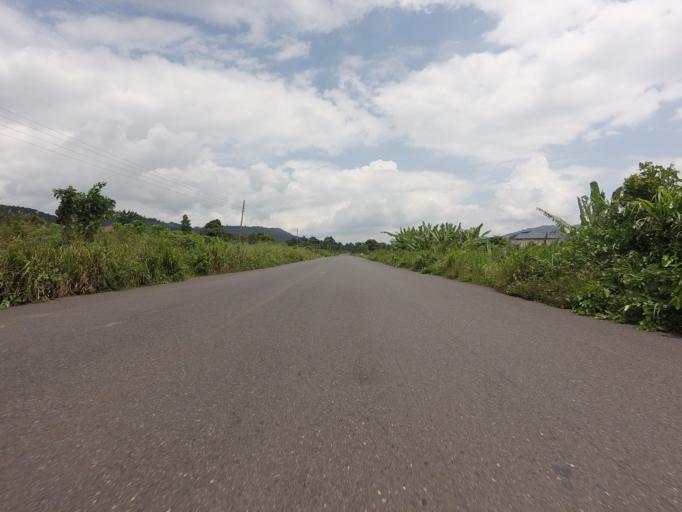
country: GH
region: Volta
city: Ho
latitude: 6.5478
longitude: 0.2530
